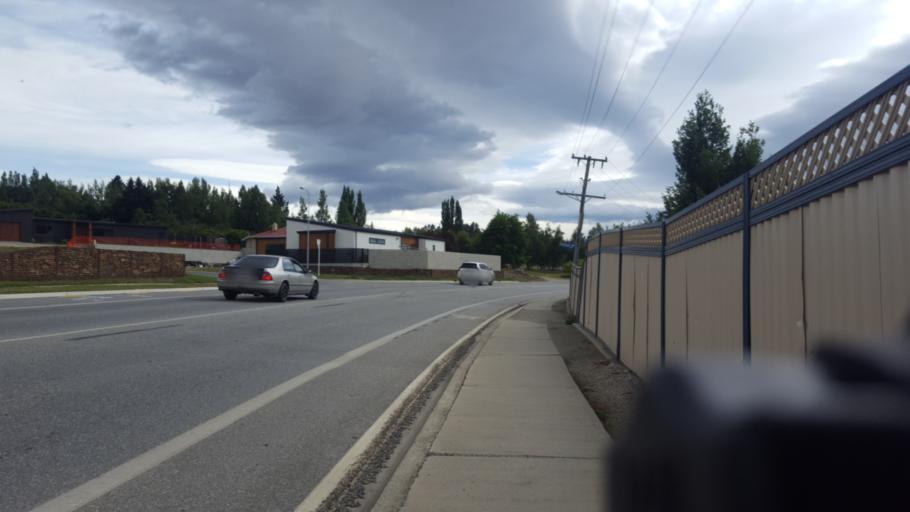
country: NZ
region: Otago
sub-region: Queenstown-Lakes District
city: Wanaka
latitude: -45.2459
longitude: 169.4024
